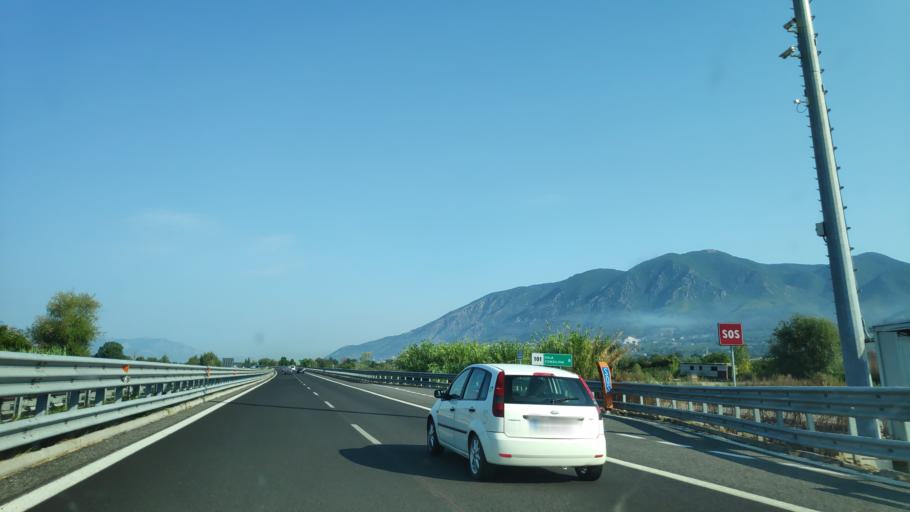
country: IT
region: Campania
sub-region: Provincia di Salerno
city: Sala Consilina
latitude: 40.3583
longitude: 15.6115
